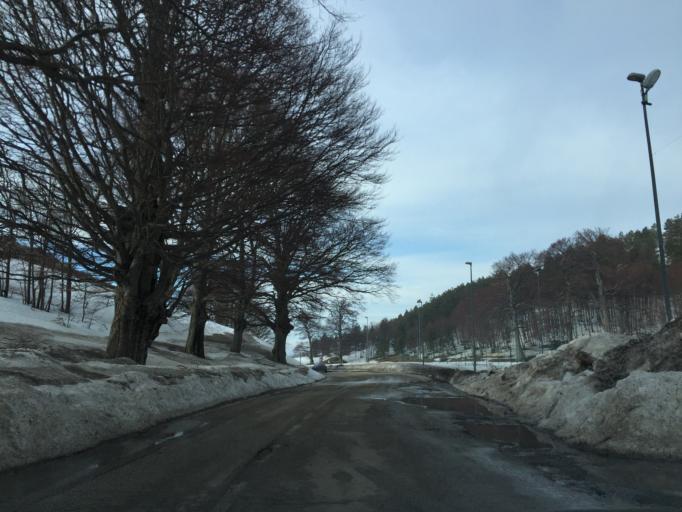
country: IT
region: Molise
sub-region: Provincia di Campobasso
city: San Massimo
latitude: 41.4632
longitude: 14.3950
